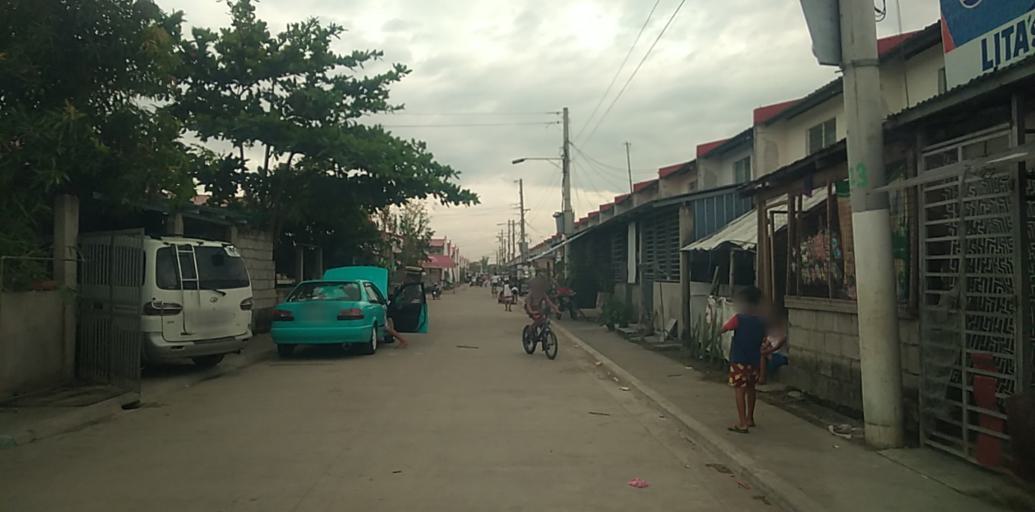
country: PH
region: Central Luzon
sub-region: Province of Pampanga
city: San Fernando
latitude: 15.0096
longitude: 120.7009
